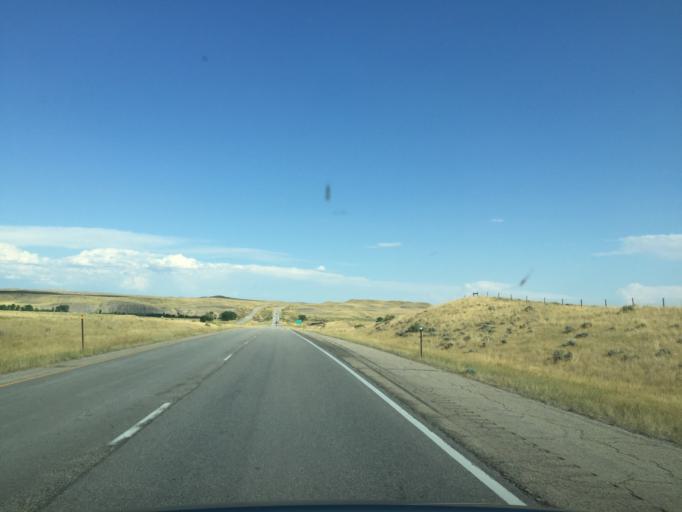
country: US
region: Wyoming
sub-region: Johnson County
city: Buffalo
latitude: 43.6317
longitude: -106.5852
